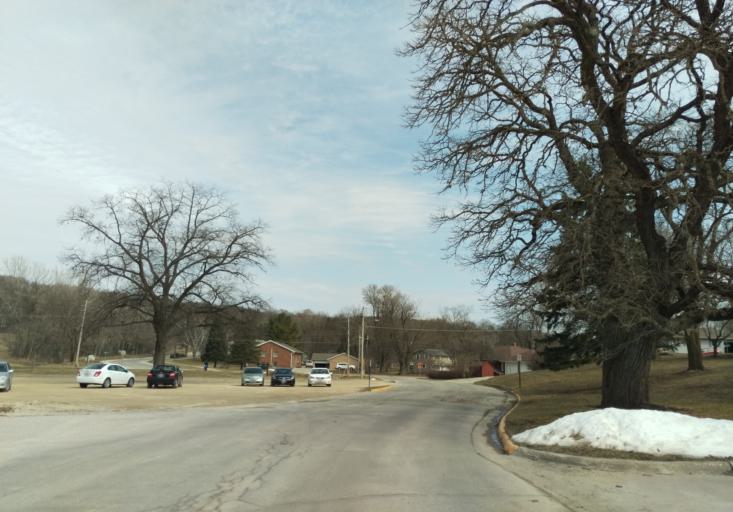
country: US
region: Iowa
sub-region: Winneshiek County
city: Decorah
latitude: 43.3132
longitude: -91.8011
